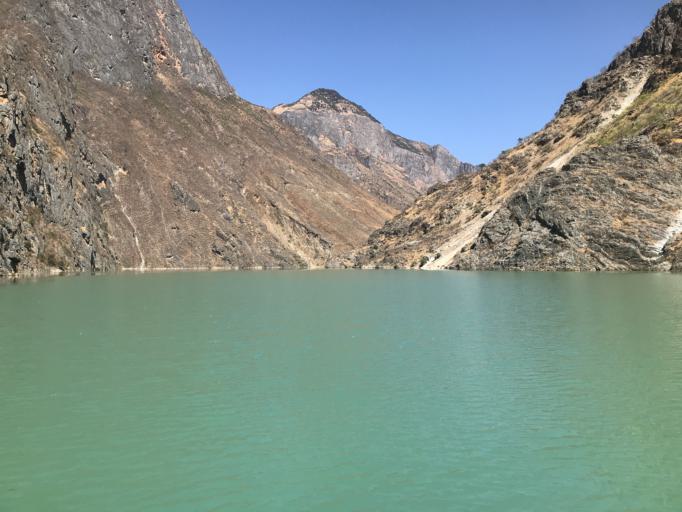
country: CN
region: Yunnan
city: Shuijia
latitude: 27.4194
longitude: 100.4622
